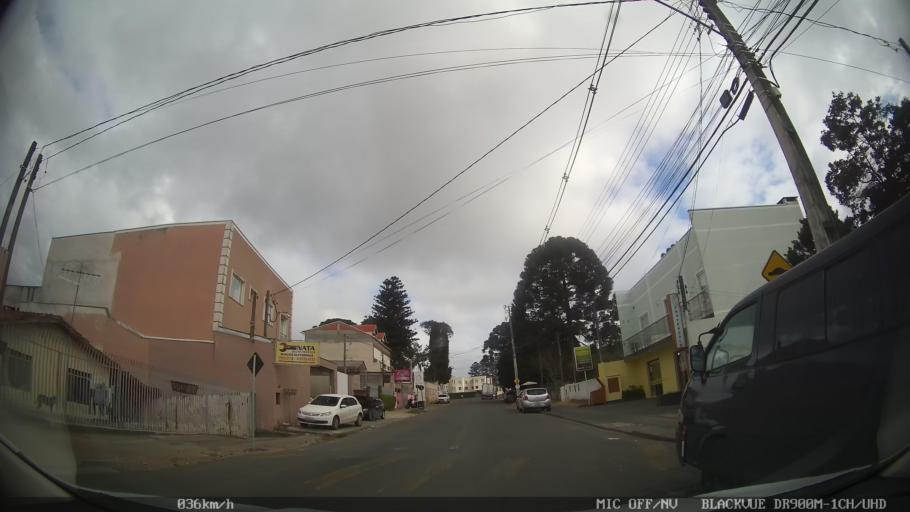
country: BR
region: Parana
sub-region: Almirante Tamandare
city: Almirante Tamandare
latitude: -25.3540
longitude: -49.2601
